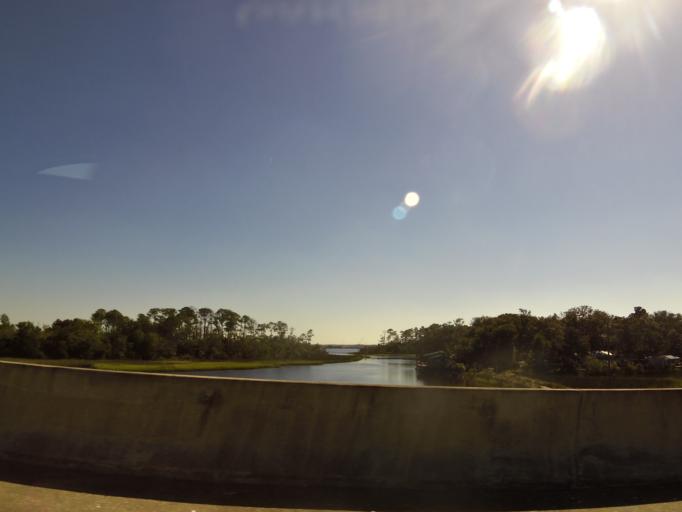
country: US
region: Florida
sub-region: Duval County
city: Jacksonville
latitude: 30.4119
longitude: -81.5495
